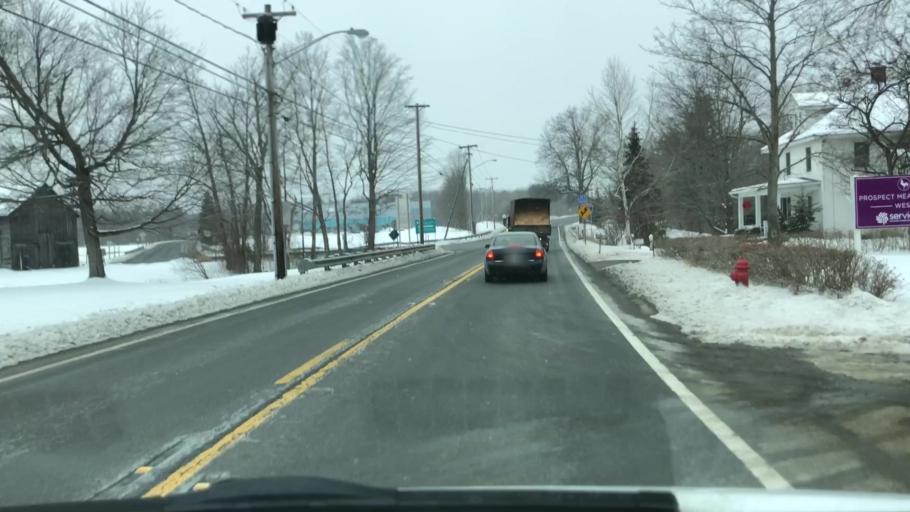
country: US
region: Massachusetts
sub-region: Franklin County
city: Whately
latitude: 42.4018
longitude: -72.6255
